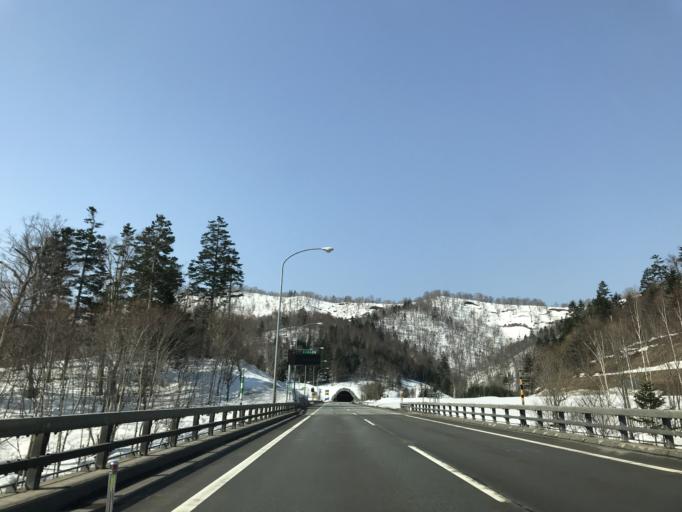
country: JP
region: Hokkaido
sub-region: Asahikawa-shi
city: Asahikawa
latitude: 43.7862
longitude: 142.2391
